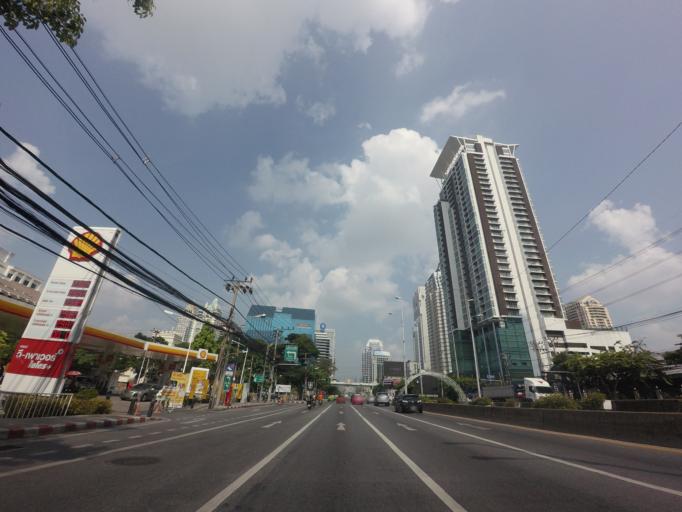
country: TH
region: Bangkok
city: Bang Rak
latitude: 13.7233
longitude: 100.5347
